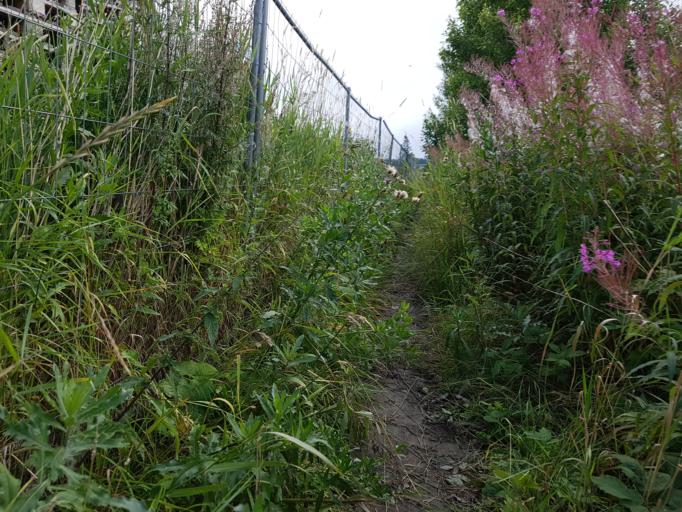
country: NO
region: Sor-Trondelag
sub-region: Trondheim
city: Trondheim
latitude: 63.4239
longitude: 10.4770
